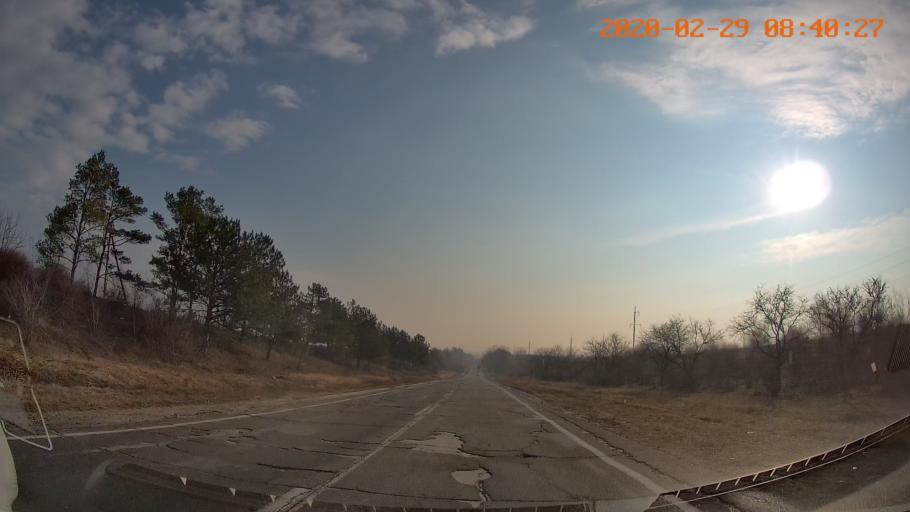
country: MD
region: Anenii Noi
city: Varnita
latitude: 46.9233
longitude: 29.4180
